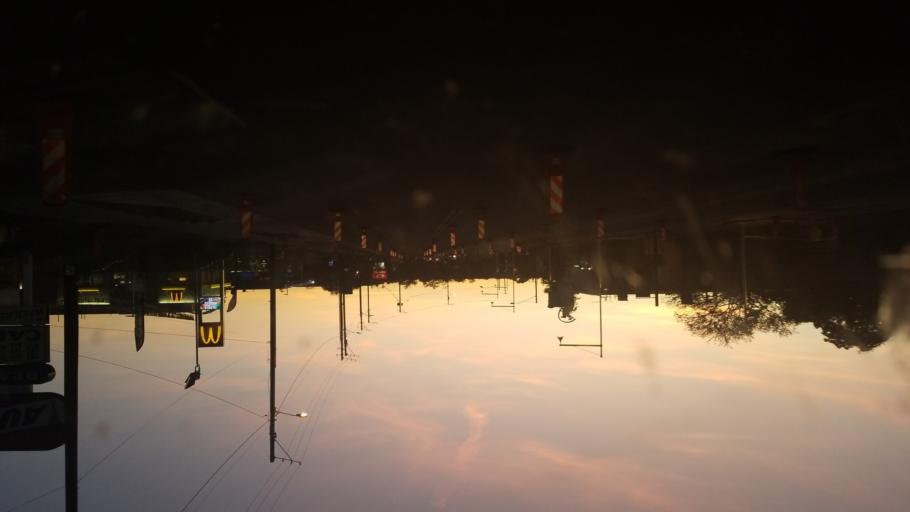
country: US
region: New Mexico
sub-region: Bernalillo County
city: Albuquerque
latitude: 35.0954
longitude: -106.6732
